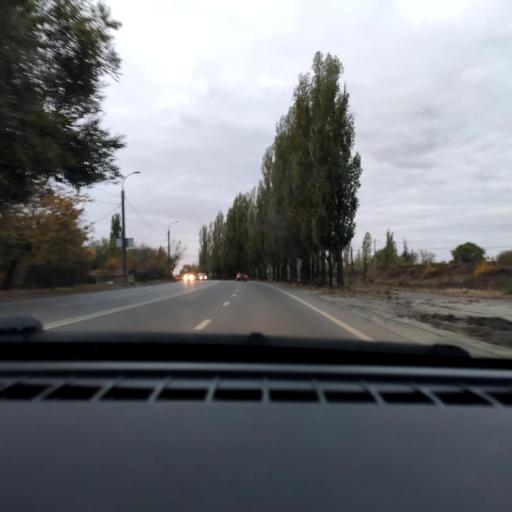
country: RU
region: Voronezj
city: Maslovka
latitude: 51.6205
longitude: 39.2596
